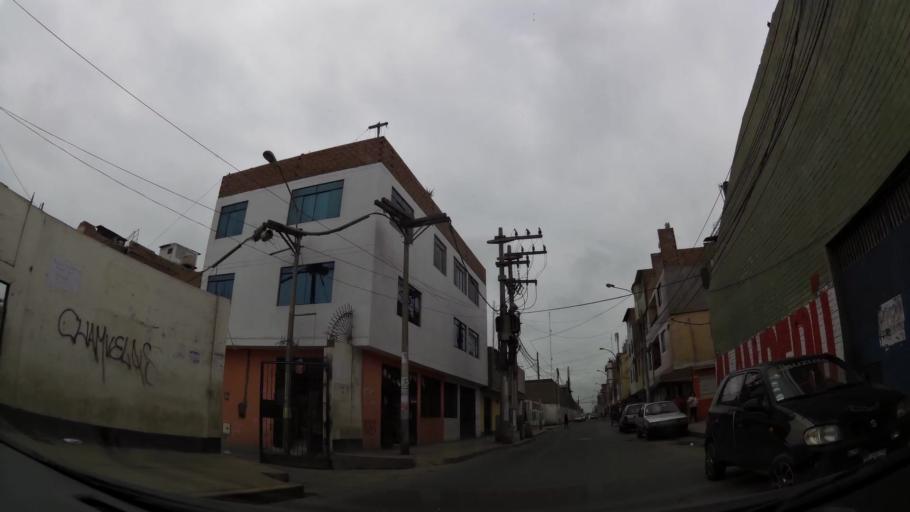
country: PE
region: Callao
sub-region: Callao
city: Callao
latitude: -12.0509
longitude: -77.1091
